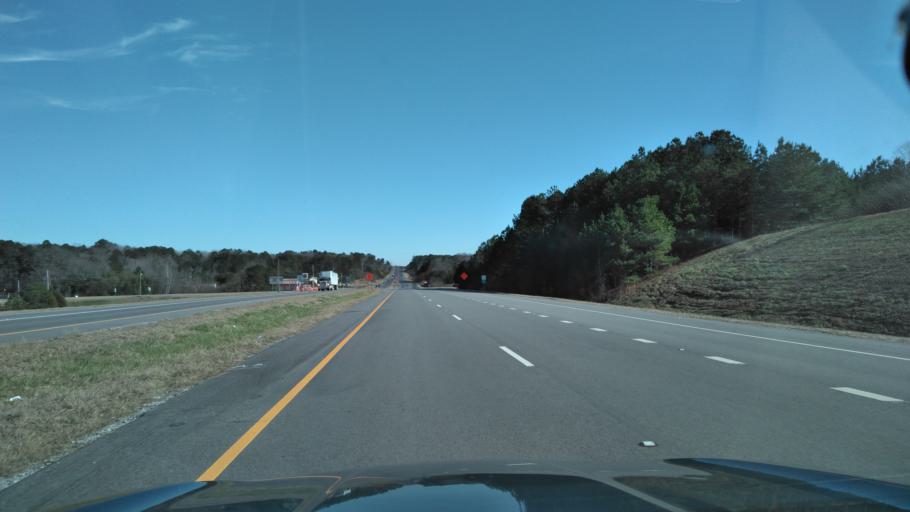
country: US
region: Alabama
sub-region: Walker County
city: Jasper
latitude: 33.8552
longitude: -87.3405
